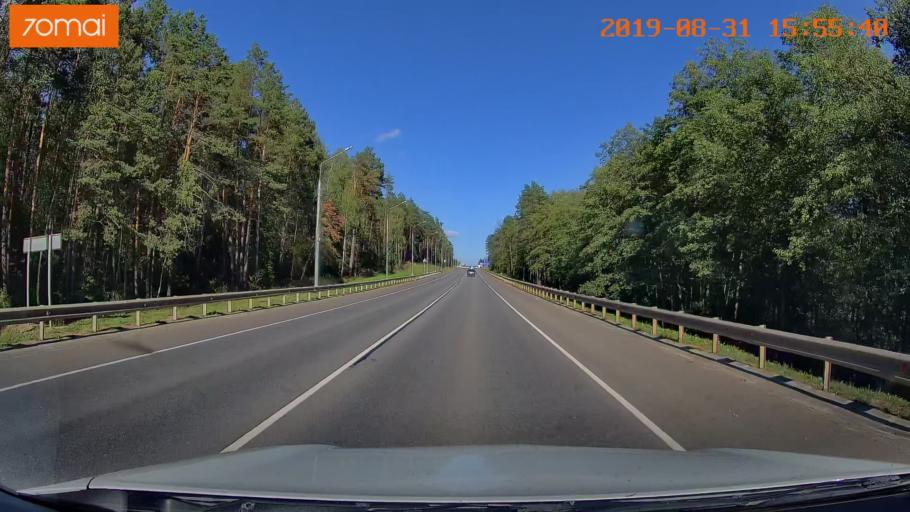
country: RU
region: Kaluga
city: Yukhnov
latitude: 54.7262
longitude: 35.1732
